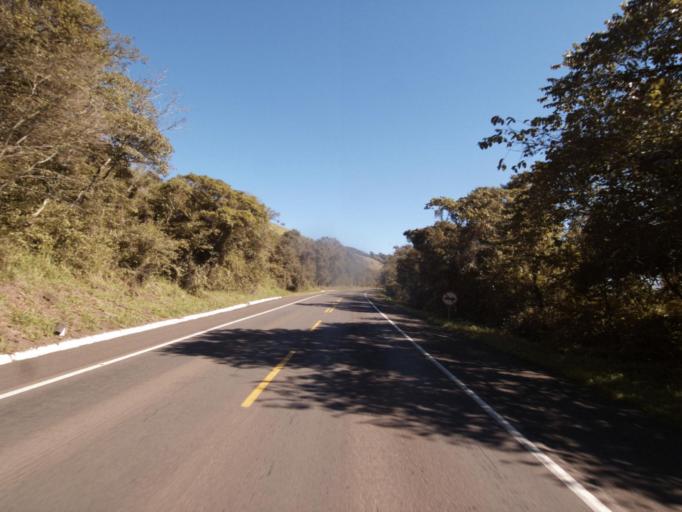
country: BR
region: Rio Grande do Sul
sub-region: Frederico Westphalen
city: Frederico Westphalen
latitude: -26.8244
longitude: -53.3946
